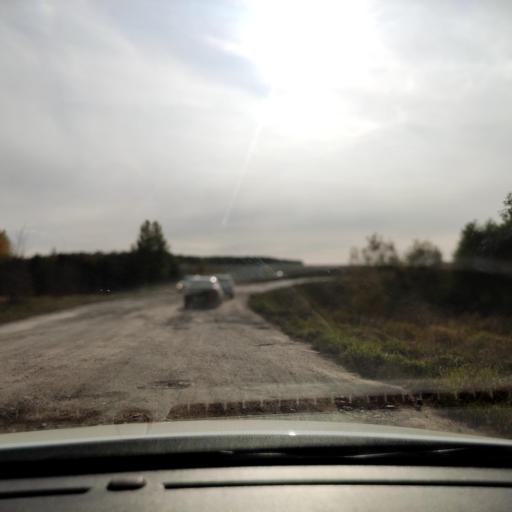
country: RU
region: Tatarstan
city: Vysokaya Gora
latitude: 55.8631
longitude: 49.3653
